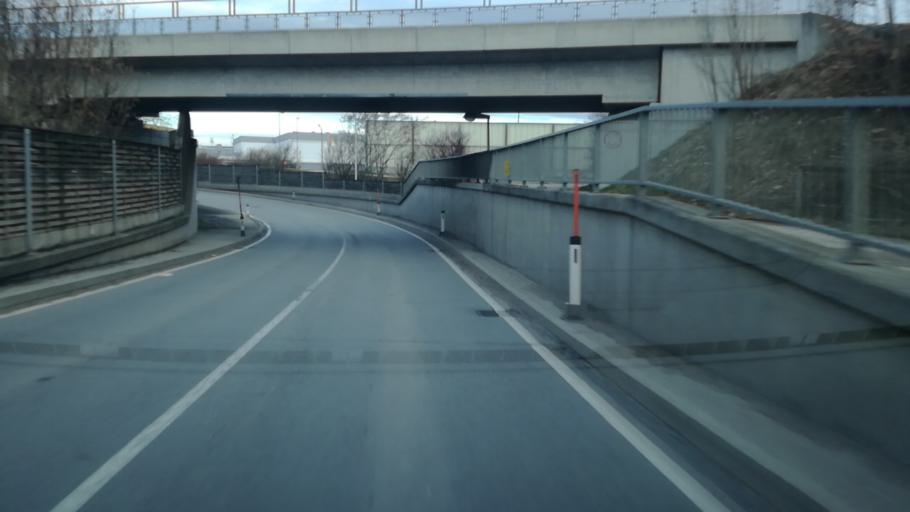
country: AT
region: Upper Austria
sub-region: Politischer Bezirk Ried im Innkreis
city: Ried im Innkreis
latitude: 48.1983
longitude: 13.4750
